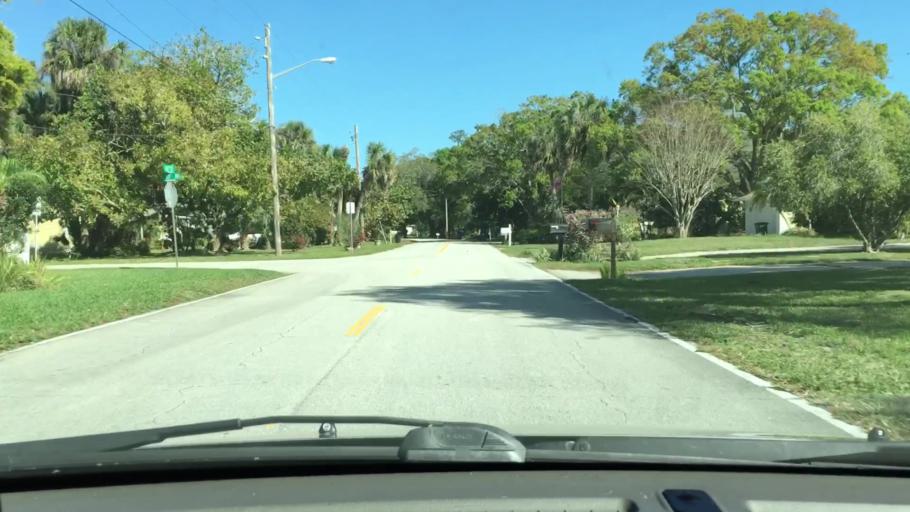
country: US
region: Florida
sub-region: Indian River County
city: Vero Beach
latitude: 27.6456
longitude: -80.3939
